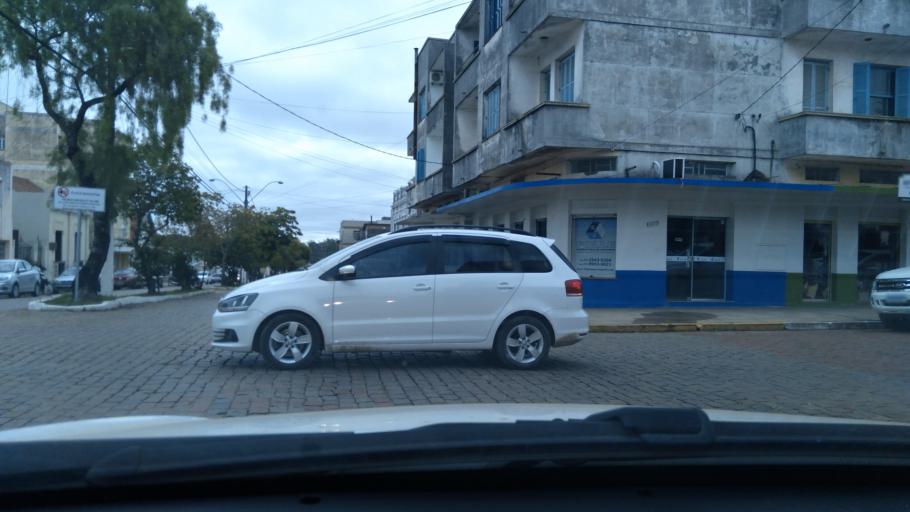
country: BR
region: Rio Grande do Sul
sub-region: Dom Pedrito
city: Dom Pedrito
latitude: -30.9842
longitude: -54.6766
